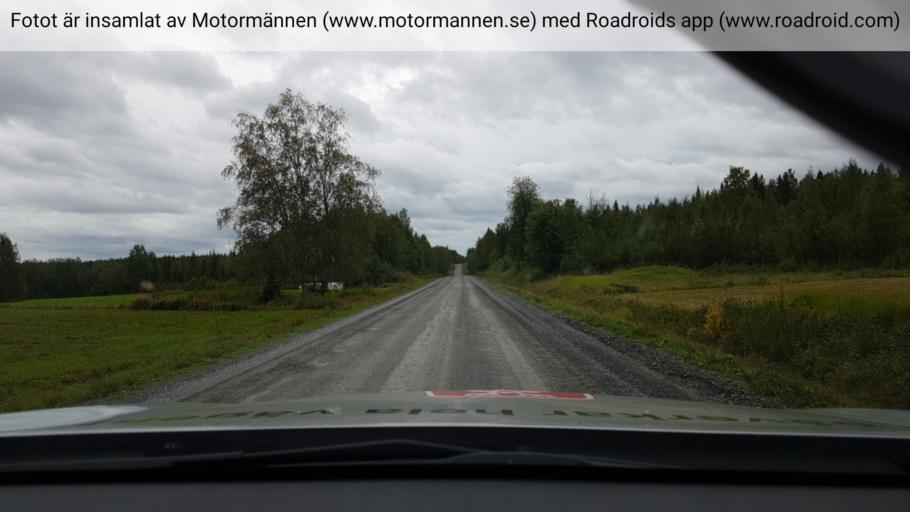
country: SE
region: Vaesterbotten
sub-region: Skelleftea Kommun
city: Forsbacka
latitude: 64.7840
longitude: 20.5134
